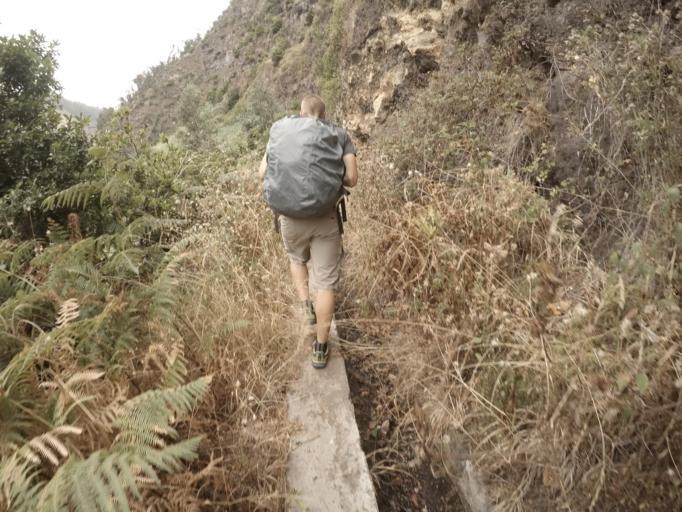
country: PT
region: Madeira
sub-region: Camara de Lobos
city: Curral das Freiras
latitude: 32.6817
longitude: -16.9583
